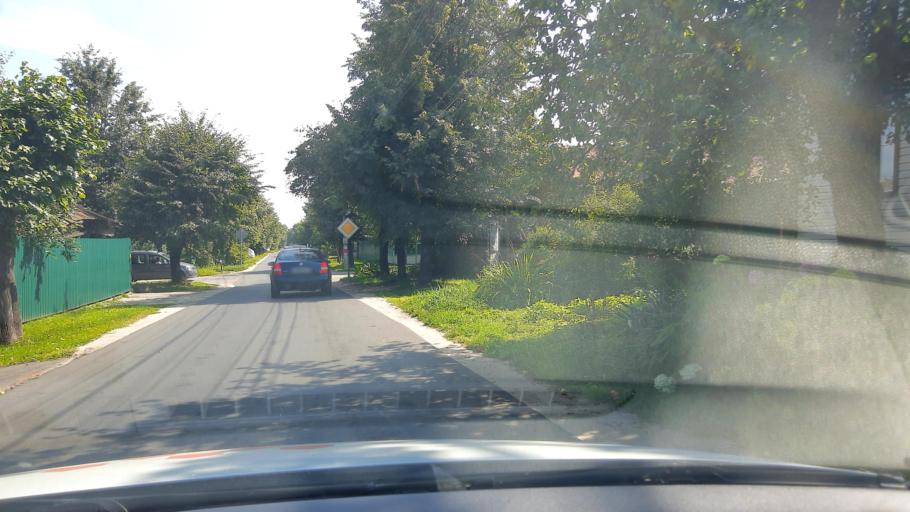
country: RU
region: Moskovskaya
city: Bronnitsy
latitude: 55.4256
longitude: 38.2567
